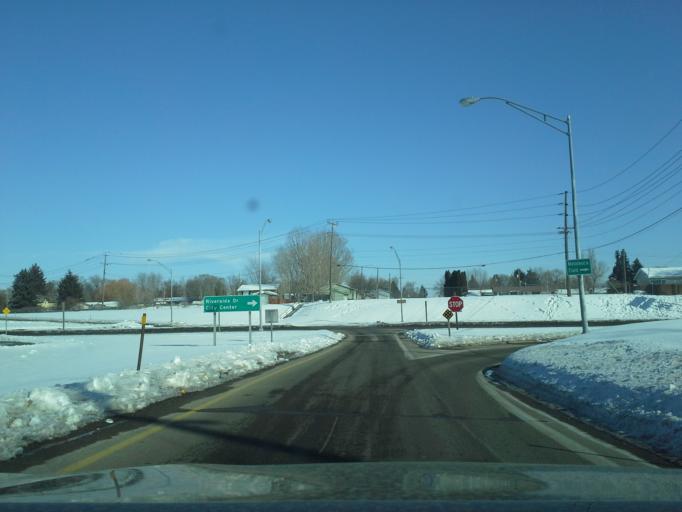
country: US
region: Idaho
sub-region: Bonneville County
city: Idaho Falls
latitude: 43.5076
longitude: -112.0478
